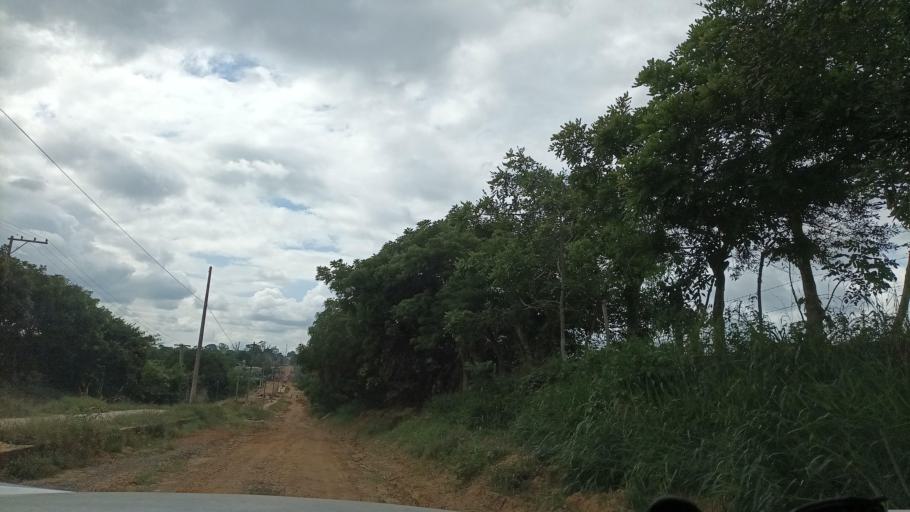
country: MX
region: Veracruz
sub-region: Soconusco
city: Fraccionamiento Santa Cruz
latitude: 17.9655
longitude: -94.8918
